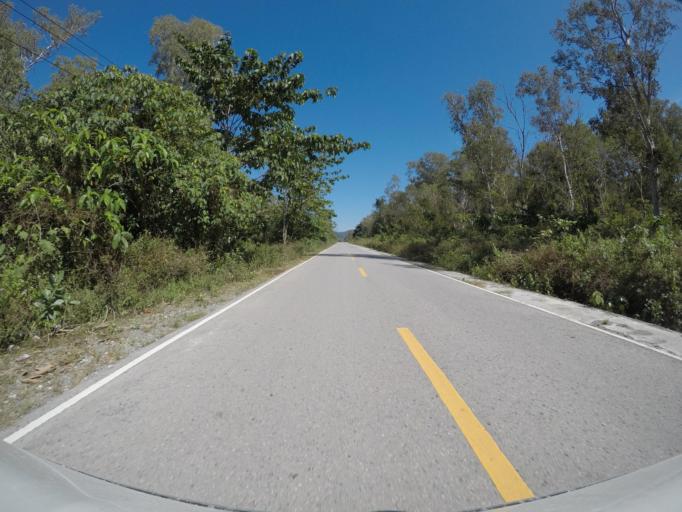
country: TL
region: Viqueque
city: Viqueque
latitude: -8.9663
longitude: 126.0229
